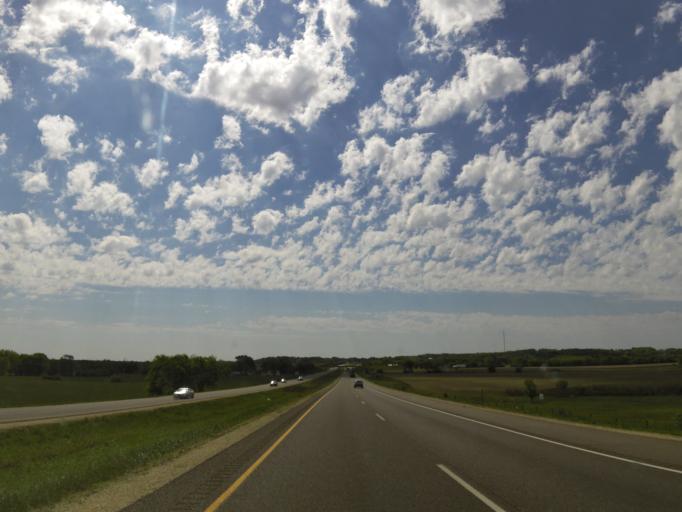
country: US
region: Wisconsin
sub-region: Eau Claire County
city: Eau Claire
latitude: 44.8267
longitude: -91.5744
